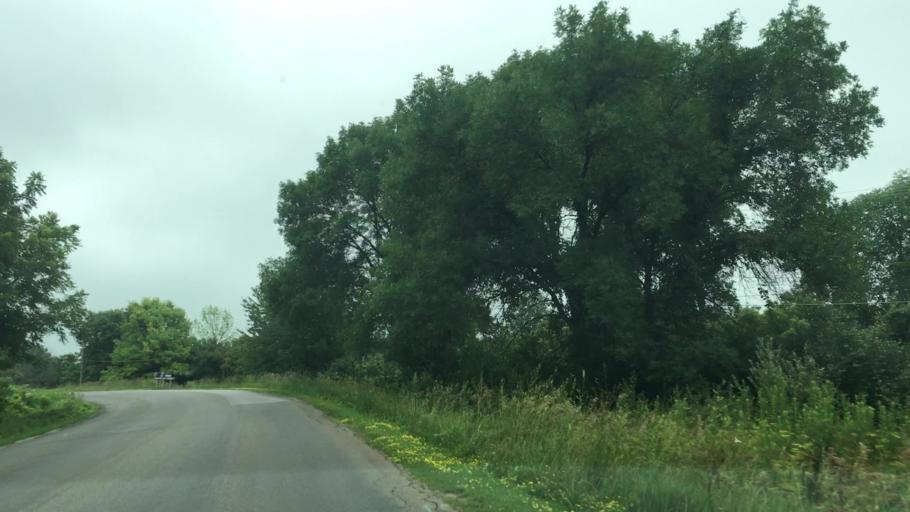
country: US
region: Iowa
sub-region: Johnson County
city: Iowa City
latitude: 41.6889
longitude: -91.5417
